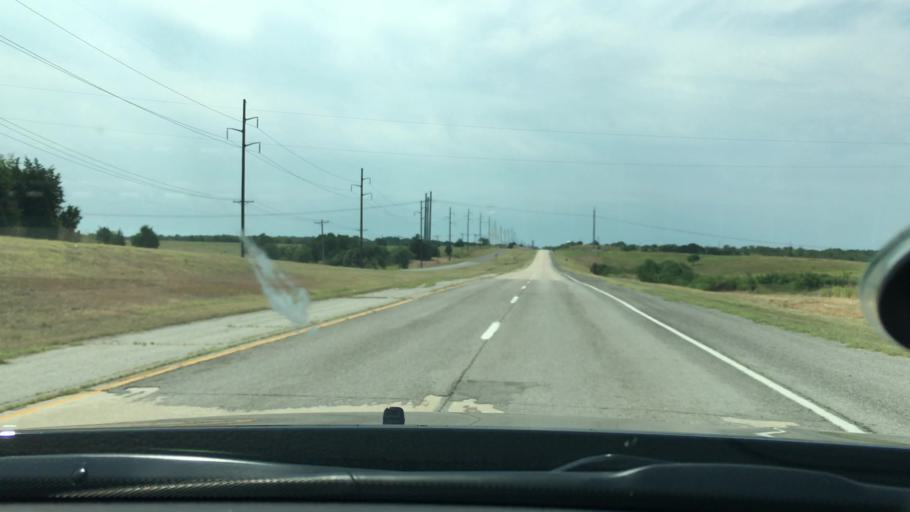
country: US
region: Oklahoma
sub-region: Carter County
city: Ardmore
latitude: 34.2375
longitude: -97.1432
